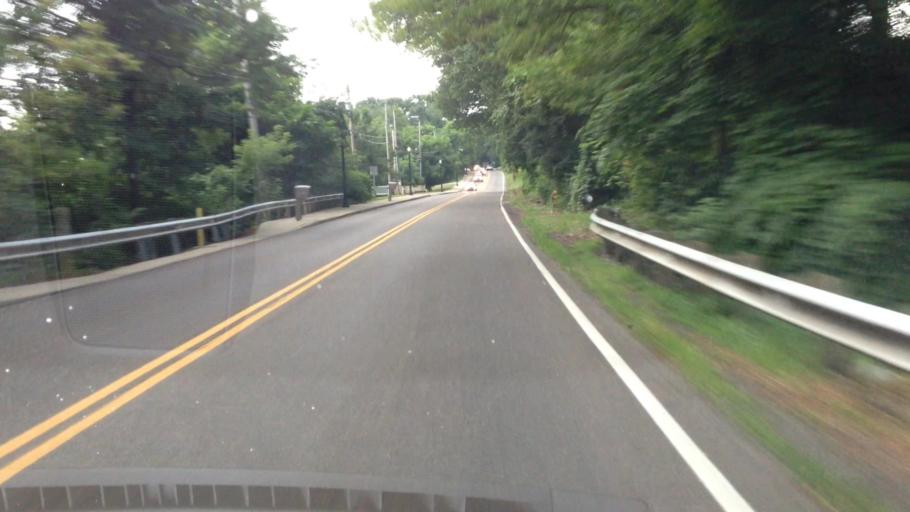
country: US
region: Ohio
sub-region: Summit County
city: Portage Lakes
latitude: 41.0018
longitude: -81.5423
